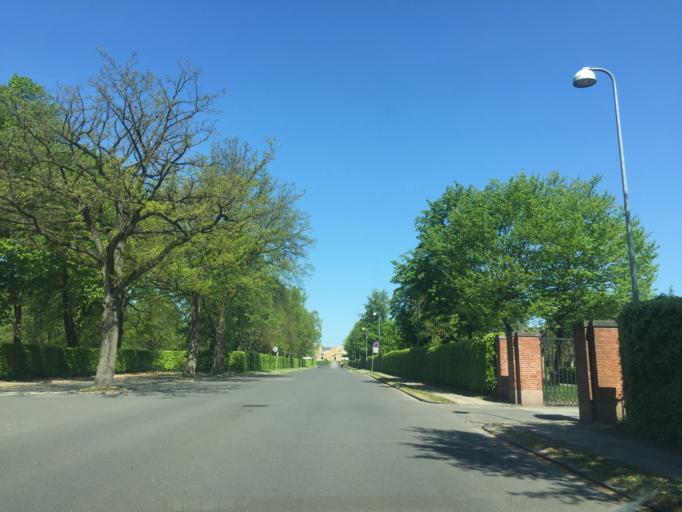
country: DK
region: South Denmark
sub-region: Odense Kommune
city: Odense
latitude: 55.3881
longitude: 10.3689
